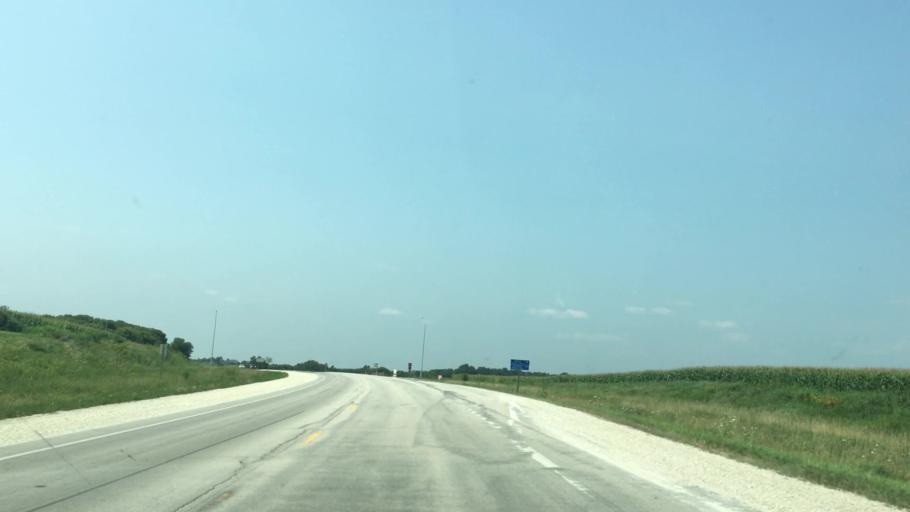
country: US
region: Iowa
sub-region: Winneshiek County
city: Decorah
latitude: 43.3661
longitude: -91.8052
